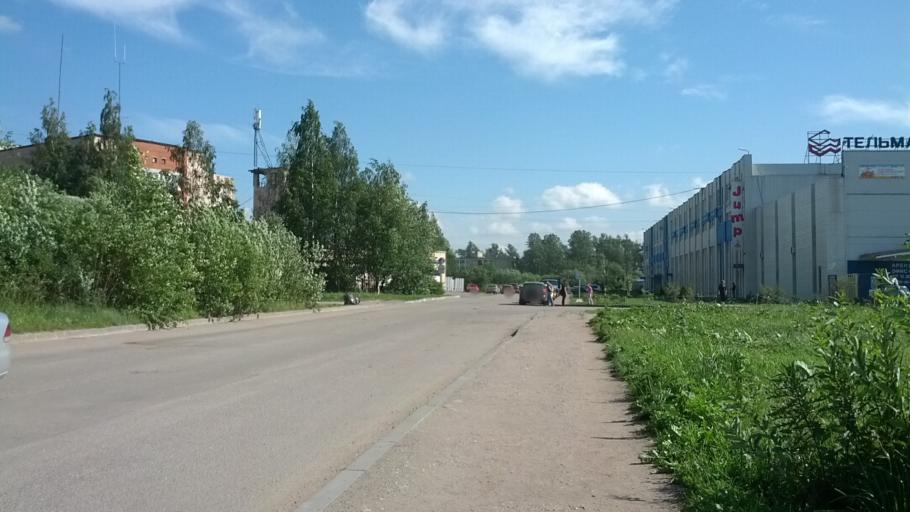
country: RU
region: Leningrad
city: Rybatskoye
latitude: 59.8905
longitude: 30.4816
